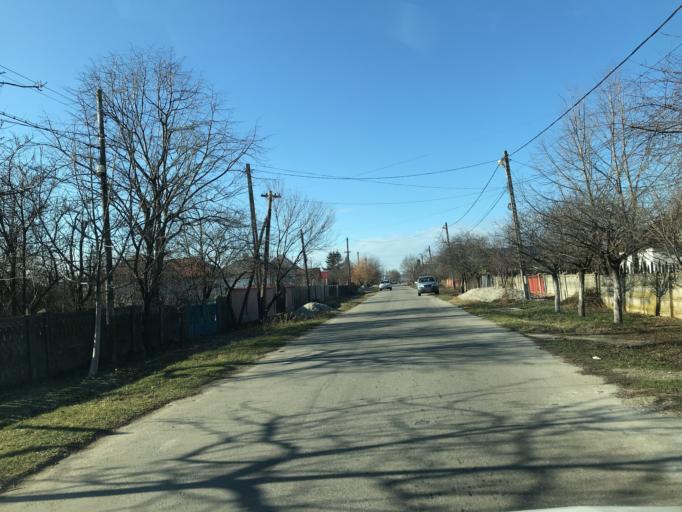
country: RO
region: Olt
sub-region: Comuna Piatra Olt
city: Piatra Olt
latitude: 44.3648
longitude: 24.2582
